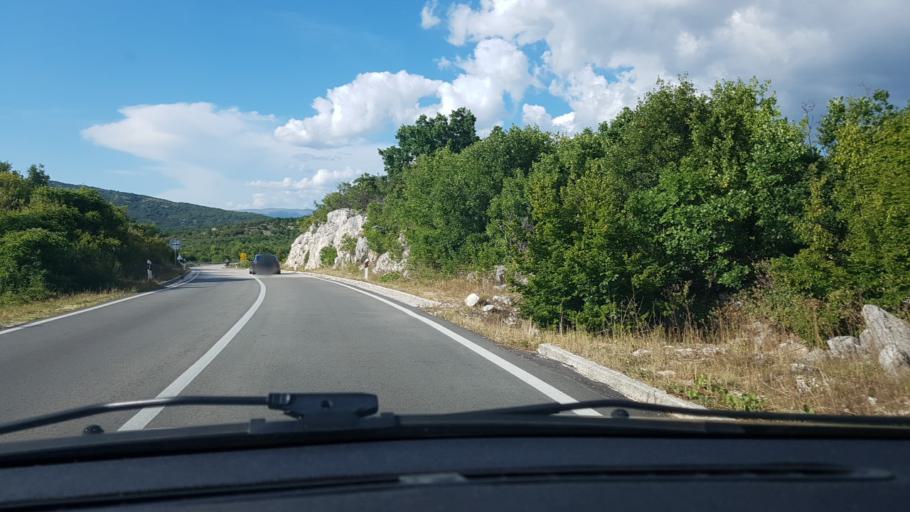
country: HR
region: Splitsko-Dalmatinska
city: Grubine
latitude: 43.4131
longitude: 17.0962
